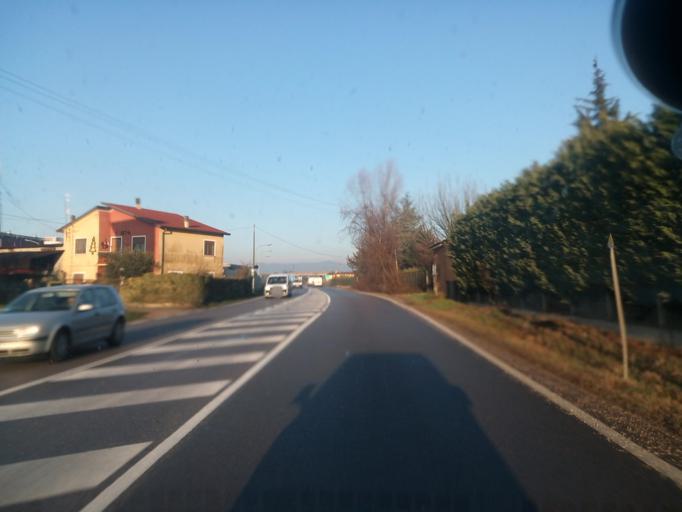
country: IT
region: Veneto
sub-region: Provincia di Vicenza
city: Monticello di Fara
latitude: 45.4336
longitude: 11.3669
